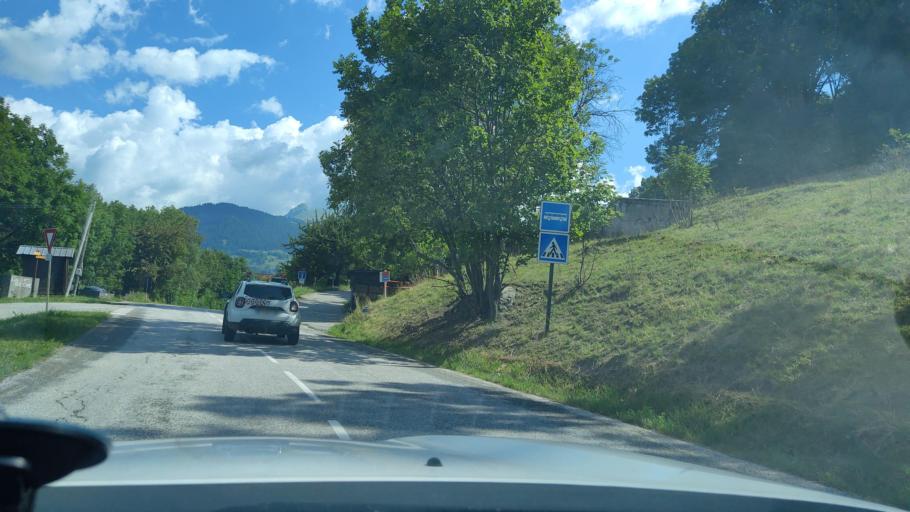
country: FR
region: Rhone-Alpes
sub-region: Departement de la Savoie
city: Bourg-Saint-Maurice
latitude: 45.6072
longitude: 6.7814
